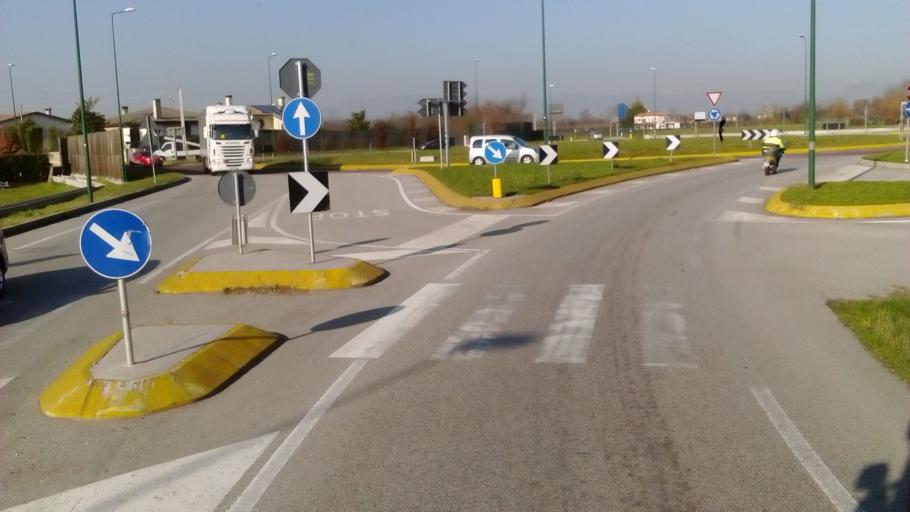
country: IT
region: Veneto
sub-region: Provincia di Treviso
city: Lancenigo-Villorba
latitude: 45.7376
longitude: 12.2781
